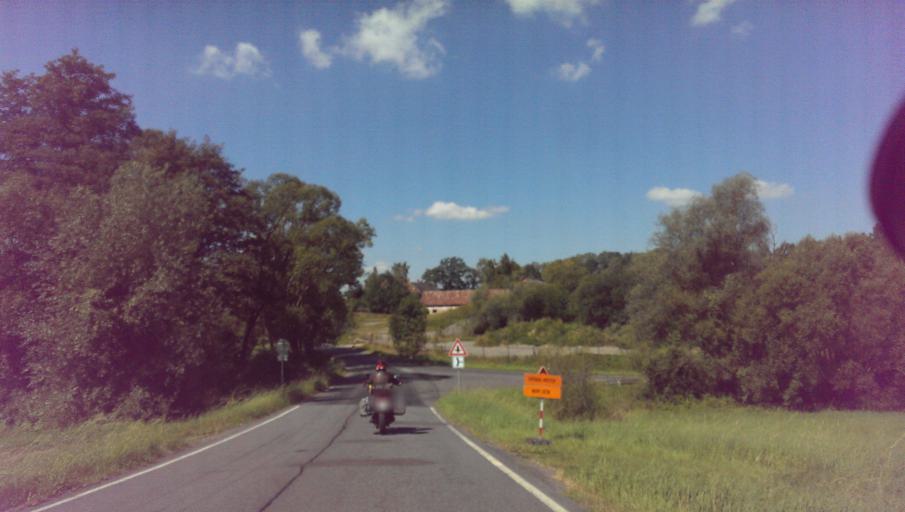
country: CZ
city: Hukvaldy
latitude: 49.6285
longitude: 18.1826
